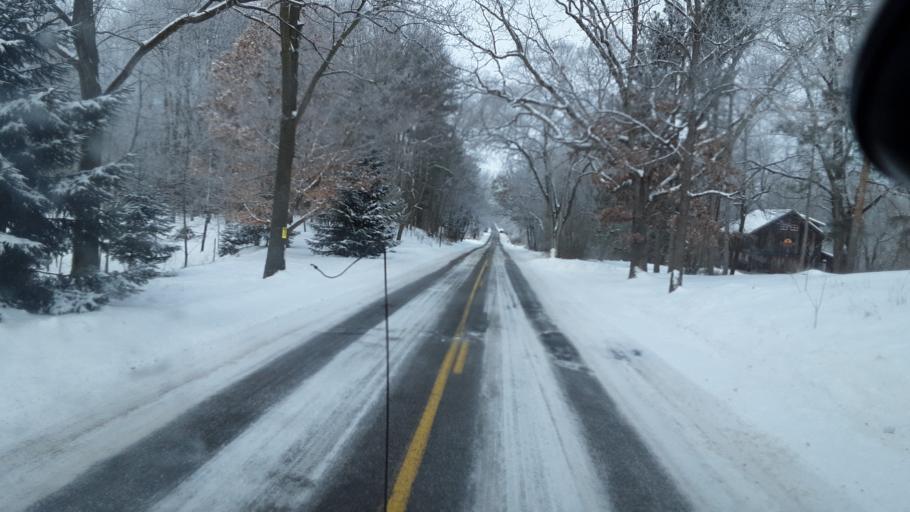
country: US
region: Michigan
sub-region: Eaton County
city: Eaton Rapids
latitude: 42.4656
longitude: -84.5548
